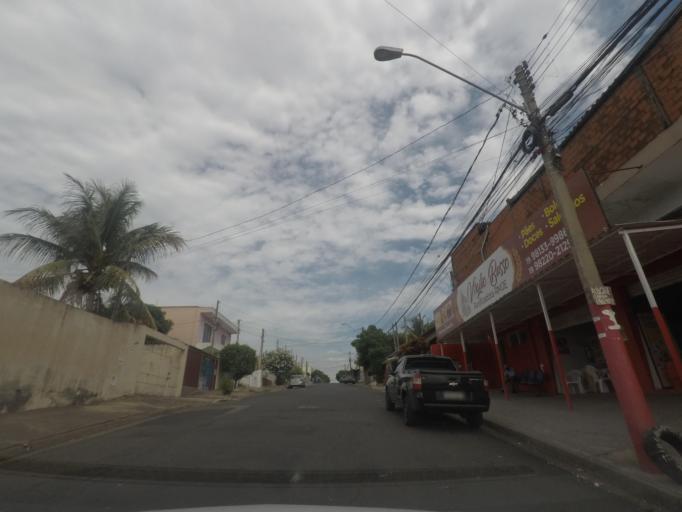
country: BR
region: Sao Paulo
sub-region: Sumare
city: Sumare
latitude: -22.8074
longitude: -47.2700
